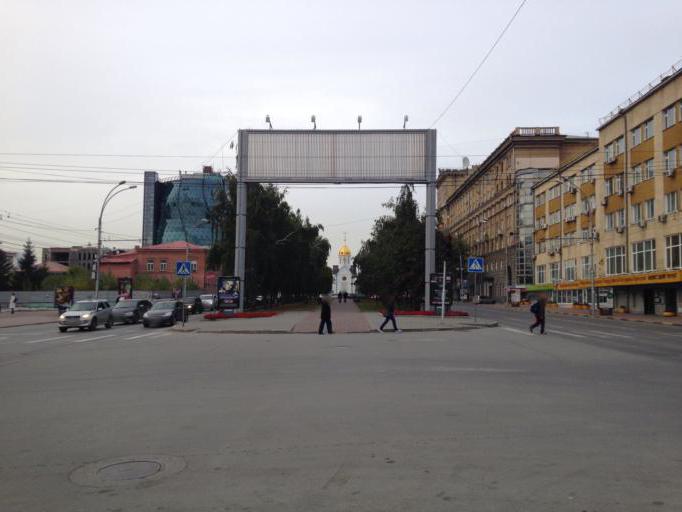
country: RU
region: Novosibirsk
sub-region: Novosibirskiy Rayon
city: Novosibirsk
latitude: 55.0247
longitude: 82.9219
